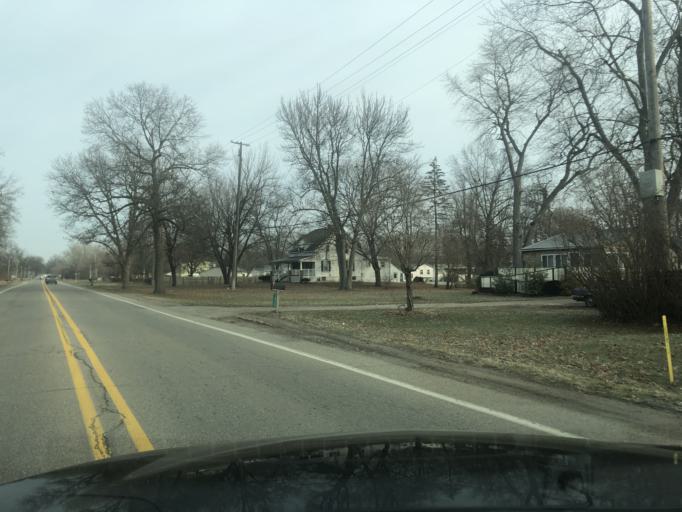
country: US
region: Michigan
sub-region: Wayne County
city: Taylor
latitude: 42.1858
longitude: -83.3257
